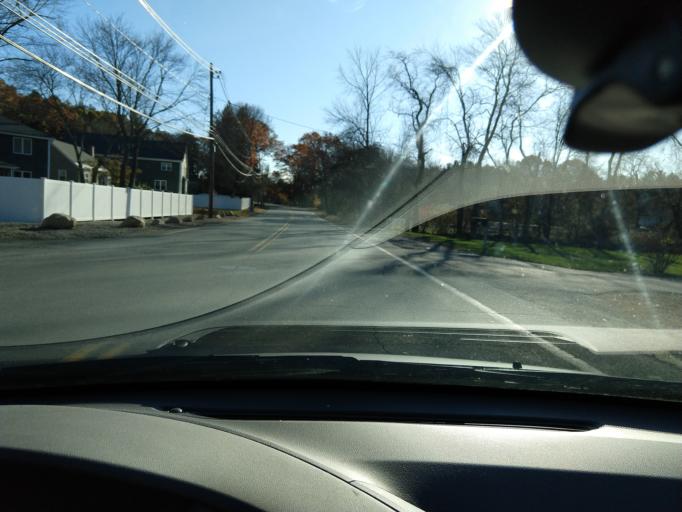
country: US
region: Massachusetts
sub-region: Middlesex County
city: Bedford
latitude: 42.5118
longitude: -71.2851
